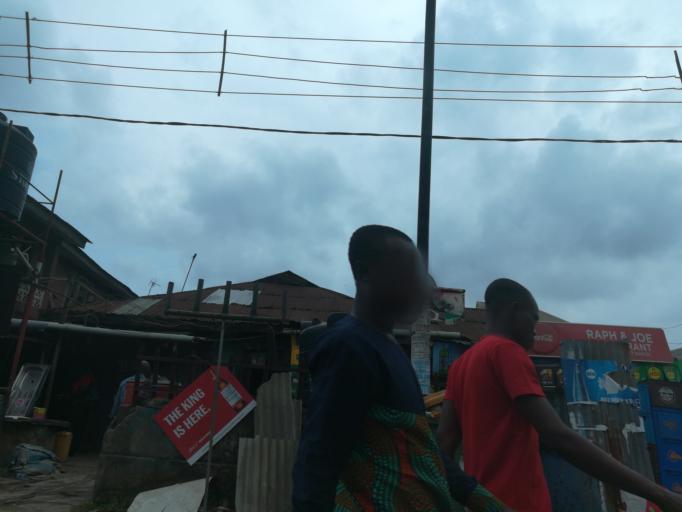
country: NG
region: Lagos
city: Oshodi
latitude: 6.5596
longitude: 3.3449
